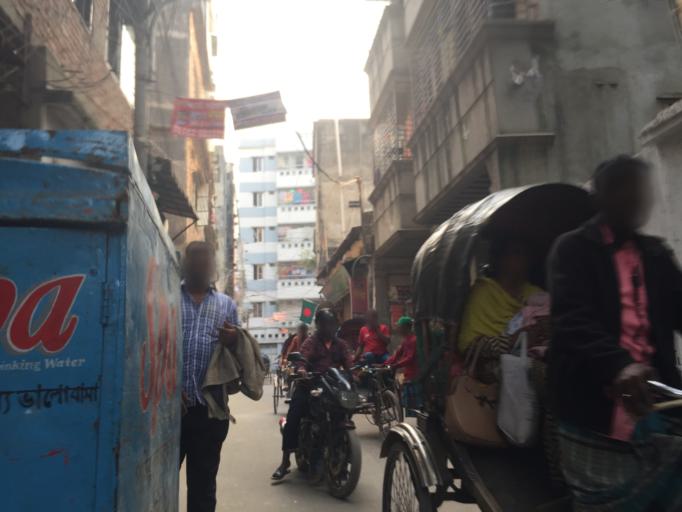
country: BD
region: Dhaka
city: Azimpur
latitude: 23.7230
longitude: 90.3821
